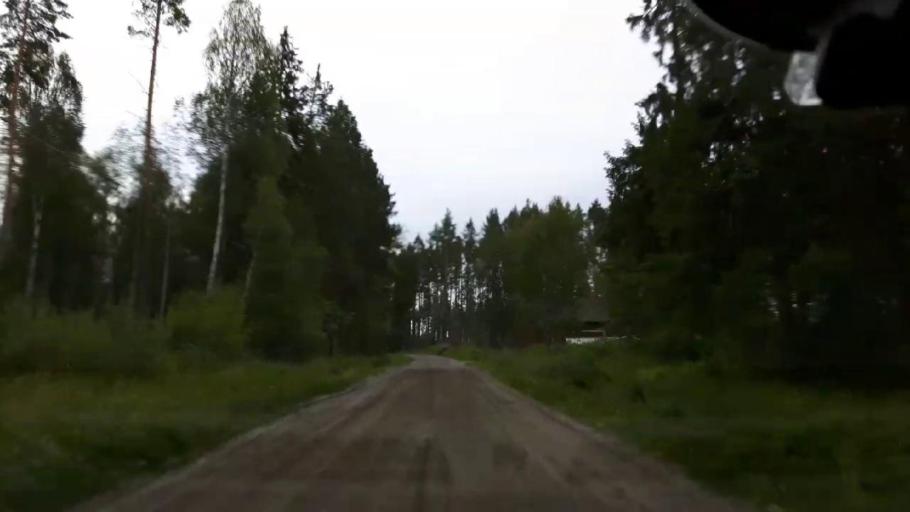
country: SE
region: Jaemtland
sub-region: Braecke Kommun
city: Braecke
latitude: 62.8922
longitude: 15.6058
